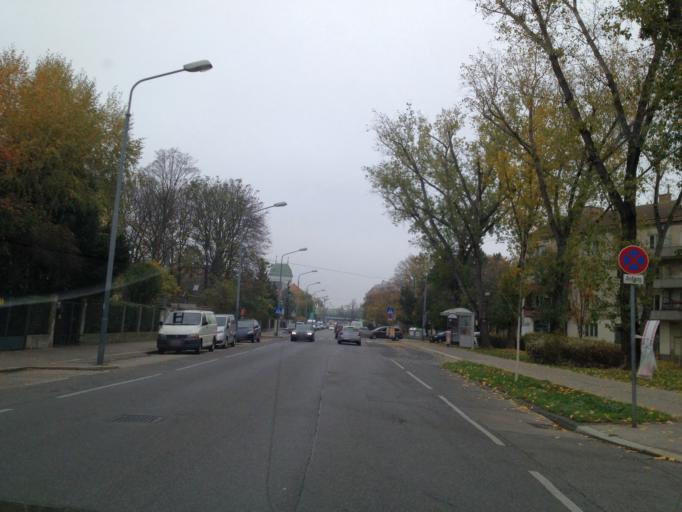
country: AT
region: Vienna
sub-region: Wien Stadt
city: Vienna
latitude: 48.2556
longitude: 16.3928
